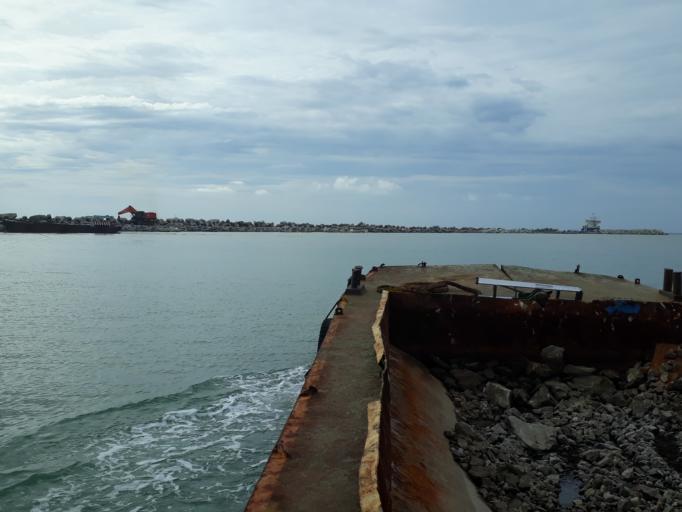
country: LK
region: Western
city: Colombo
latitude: 6.9273
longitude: 79.8233
